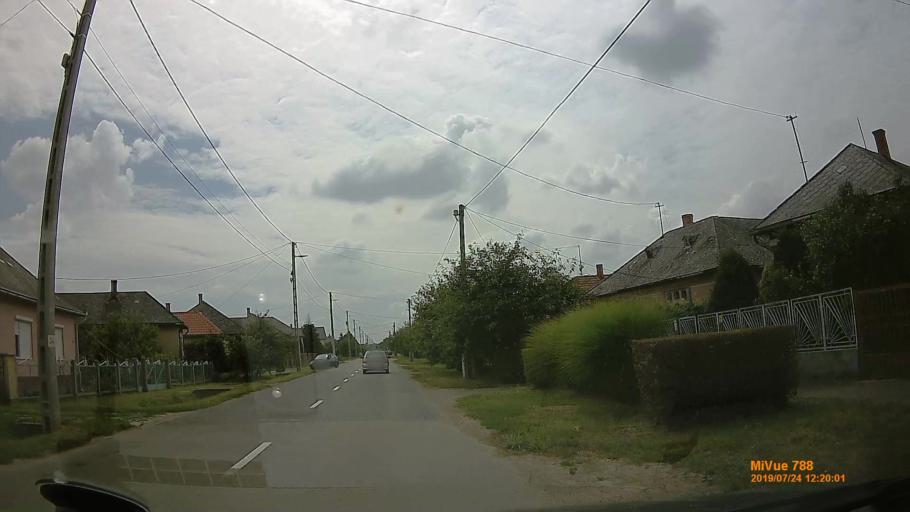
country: HU
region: Szabolcs-Szatmar-Bereg
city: Vasarosnameny
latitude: 48.1385
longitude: 22.3429
